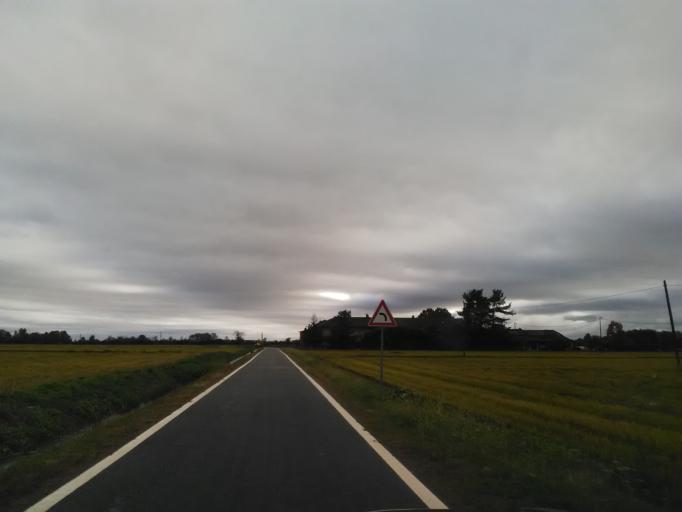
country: IT
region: Piedmont
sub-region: Provincia di Vercelli
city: Casanova Elvo
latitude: 45.4069
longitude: 8.2542
